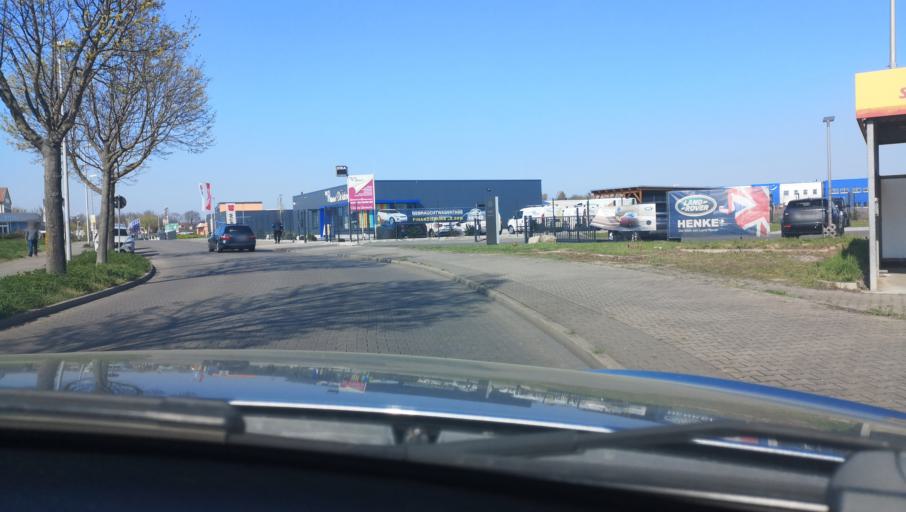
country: DE
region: Saxony-Anhalt
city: Diesdorf
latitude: 52.0806
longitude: 11.5827
